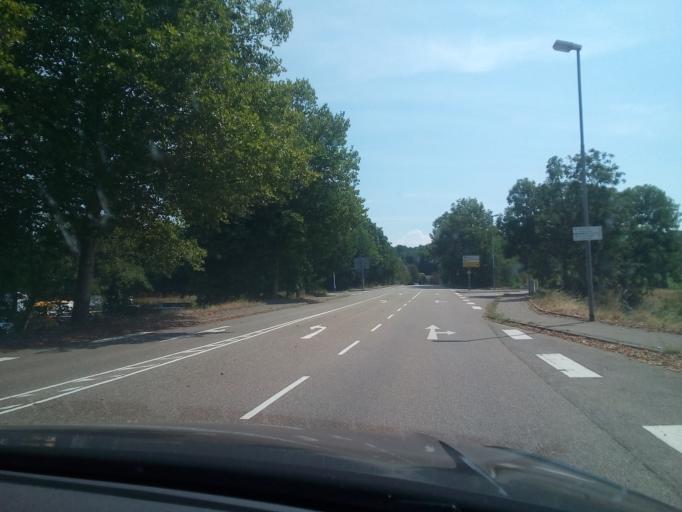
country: DE
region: Baden-Wuerttemberg
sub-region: Freiburg Region
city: Kippenheim
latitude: 48.3273
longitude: 7.8339
